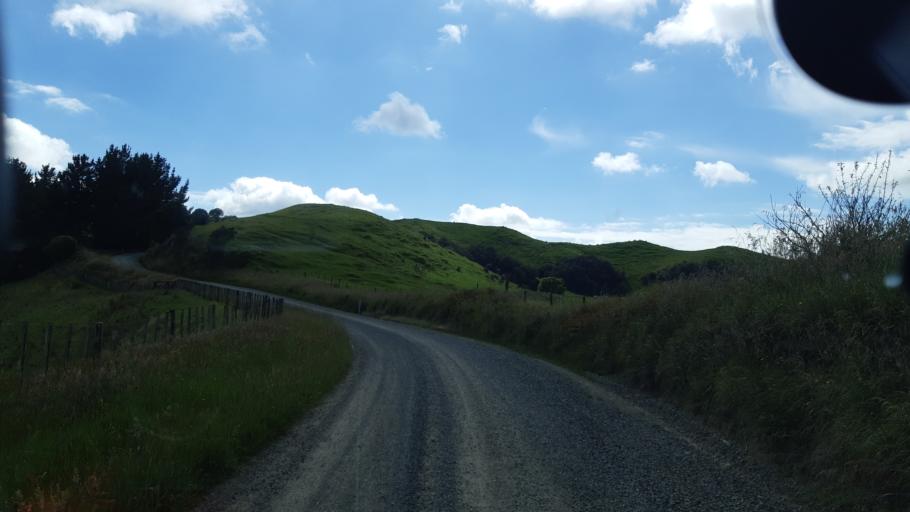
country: NZ
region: Manawatu-Wanganui
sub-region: Rangitikei District
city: Bulls
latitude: -39.9613
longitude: 175.4808
